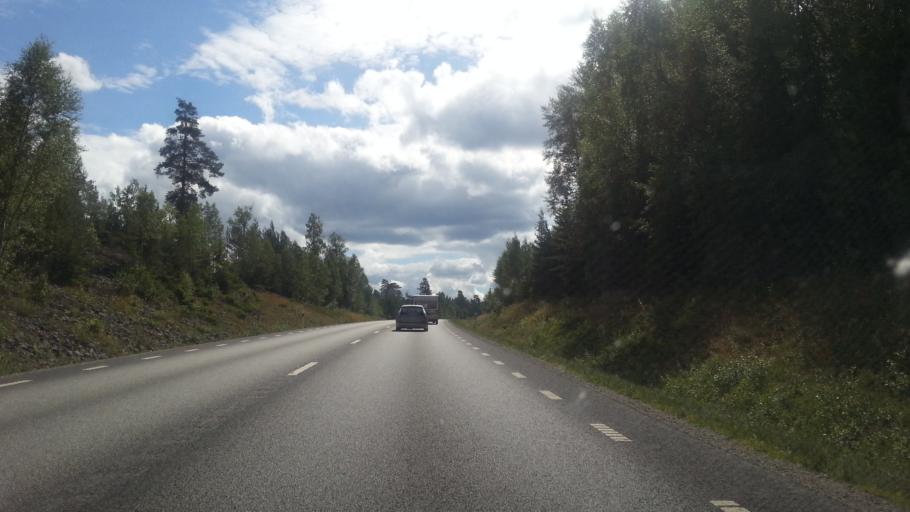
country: SE
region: OErebro
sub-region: Lindesbergs Kommun
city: Lindesberg
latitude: 59.5667
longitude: 15.2145
